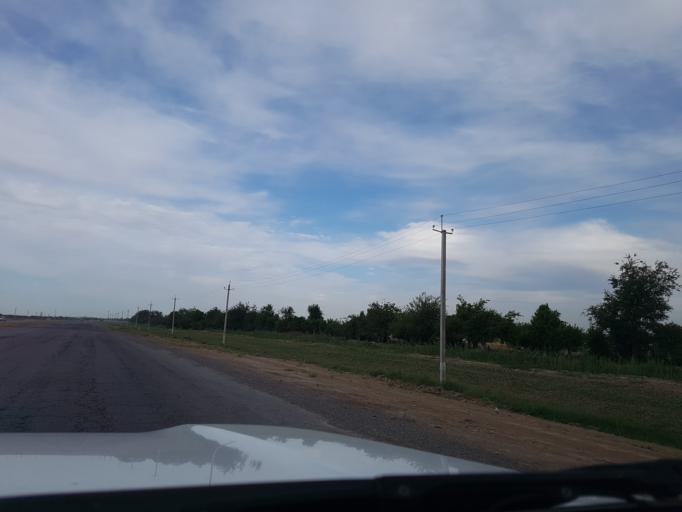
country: TM
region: Mary
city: Bayramaly
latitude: 37.6118
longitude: 62.2819
